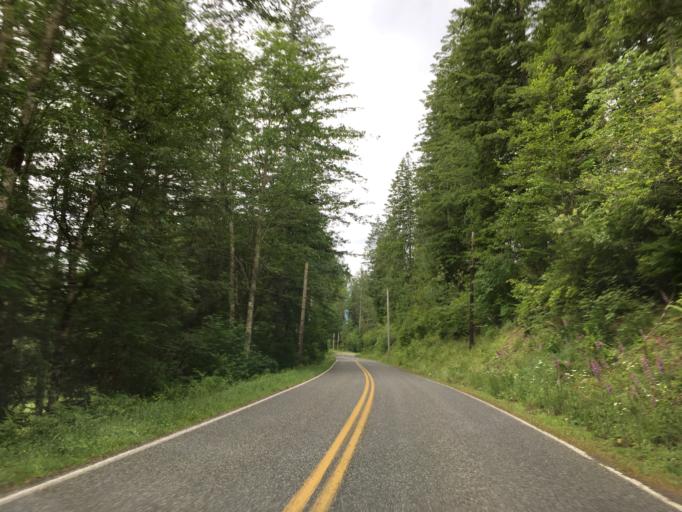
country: US
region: Washington
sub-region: Whatcom County
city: Peaceful Valley
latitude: 48.9763
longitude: -122.1384
